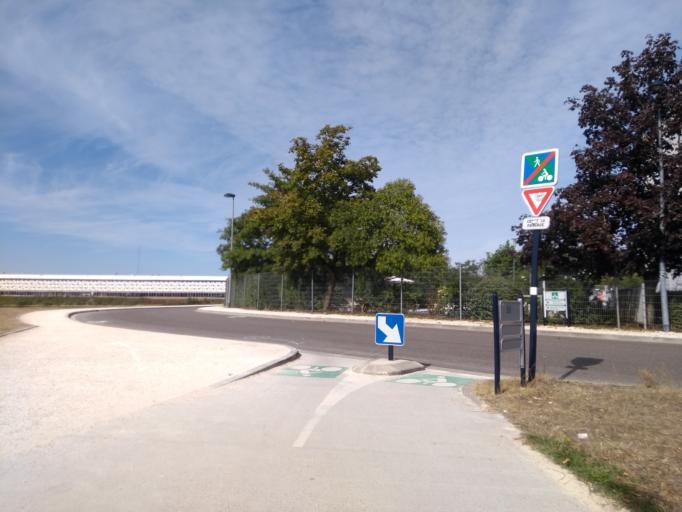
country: FR
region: Aquitaine
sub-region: Departement de la Gironde
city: Le Bouscat
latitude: 44.8905
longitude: -0.5669
